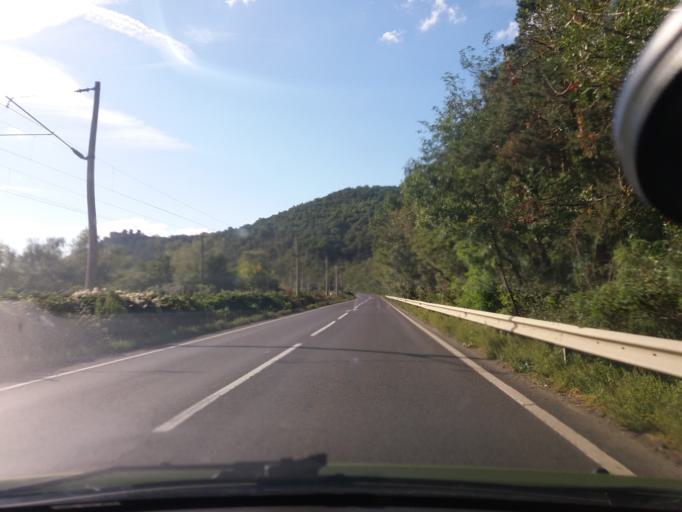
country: RO
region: Arad
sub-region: Oras Lipova
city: Lipova
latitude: 46.1076
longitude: 21.7378
